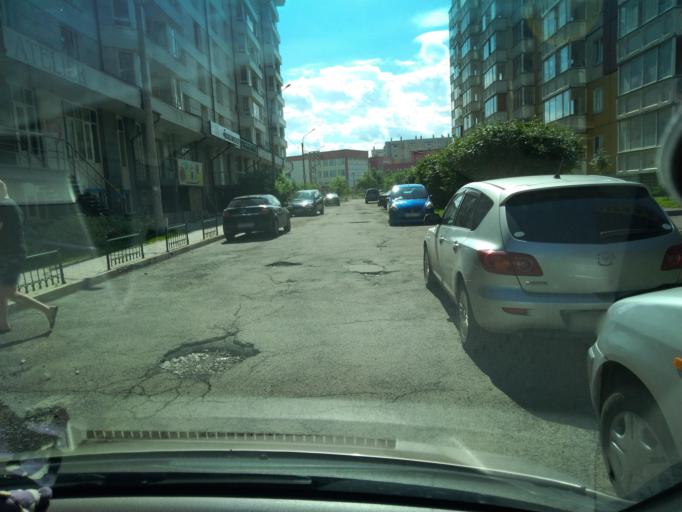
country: RU
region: Krasnoyarskiy
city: Krasnoyarsk
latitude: 56.0451
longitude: 92.9018
